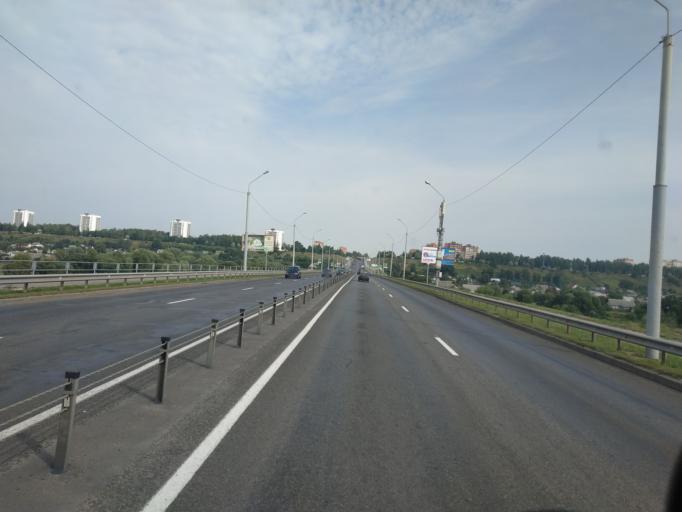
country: BY
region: Mogilev
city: Mahilyow
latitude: 53.8939
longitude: 30.3733
